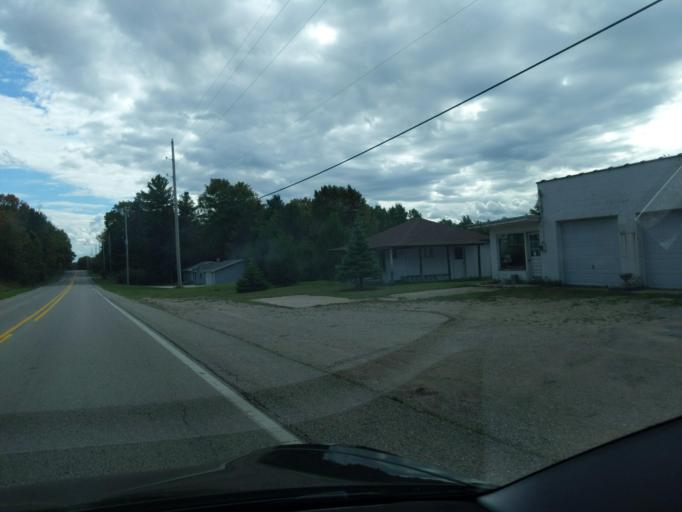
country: US
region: Michigan
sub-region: Kalkaska County
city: Rapid City
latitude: 44.9167
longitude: -85.2853
